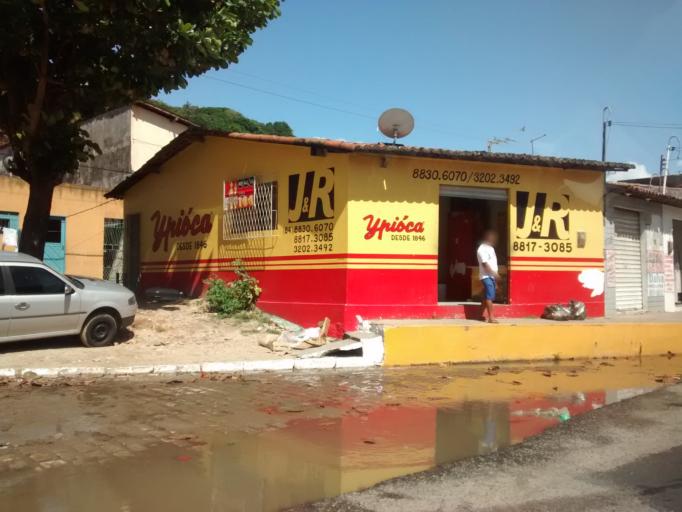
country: BR
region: Rio Grande do Norte
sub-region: Natal
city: Natal
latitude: -5.7966
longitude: -35.1872
